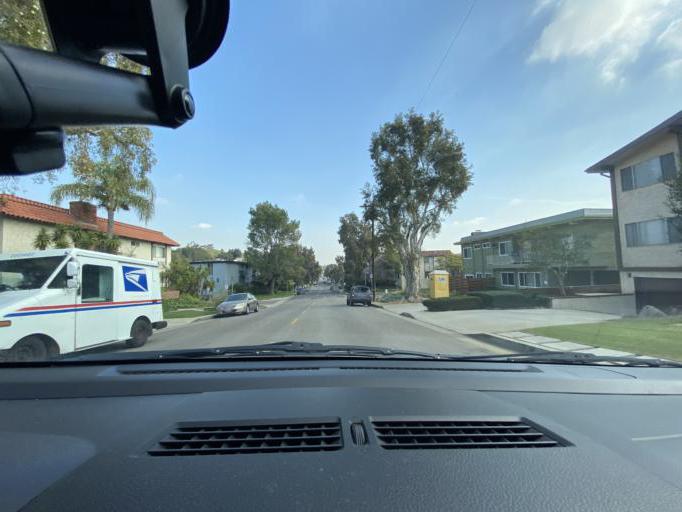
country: US
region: California
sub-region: Los Angeles County
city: Culver City
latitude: 34.0236
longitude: -118.4195
